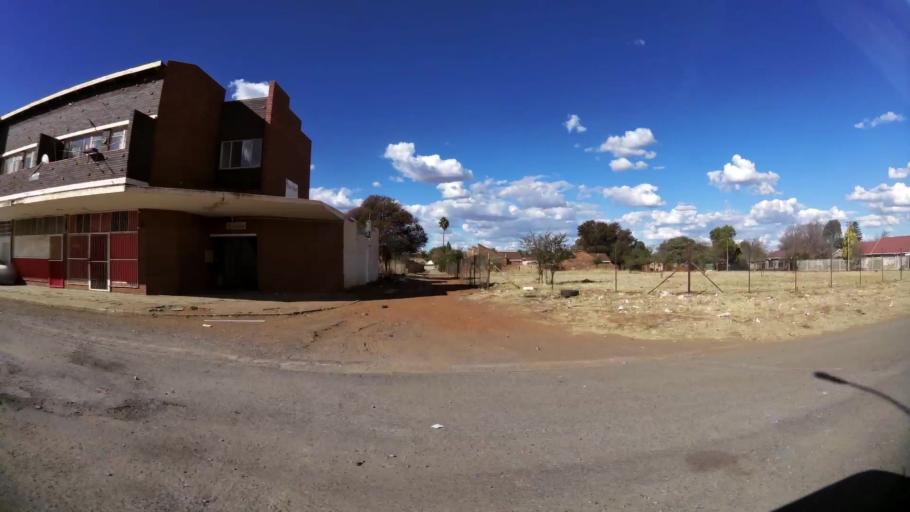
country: ZA
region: North-West
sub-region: Dr Kenneth Kaunda District Municipality
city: Klerksdorp
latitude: -26.8261
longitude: 26.6582
